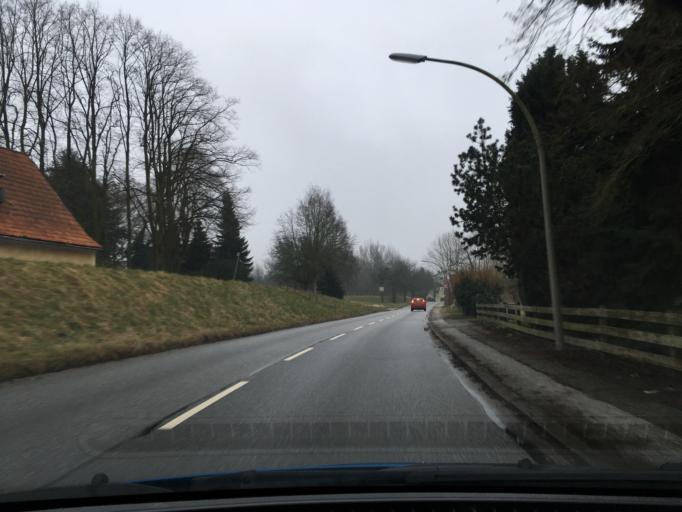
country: DE
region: Hamburg
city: Altona
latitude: 53.4942
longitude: 9.9307
